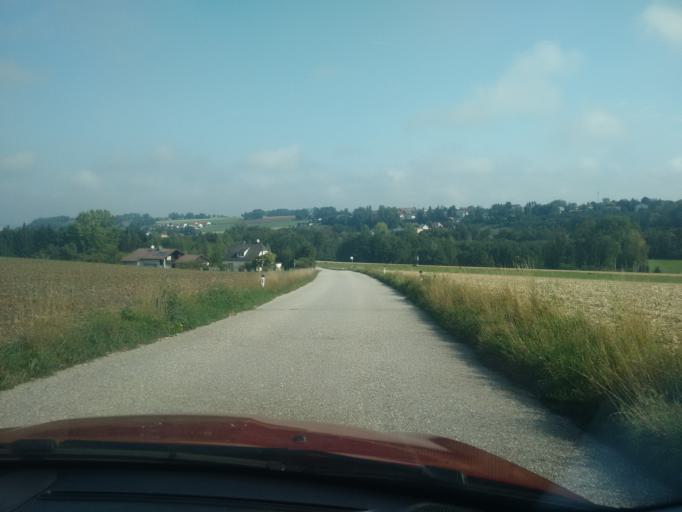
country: AT
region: Upper Austria
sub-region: Wels-Land
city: Steinhaus
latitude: 48.1168
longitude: 14.0075
